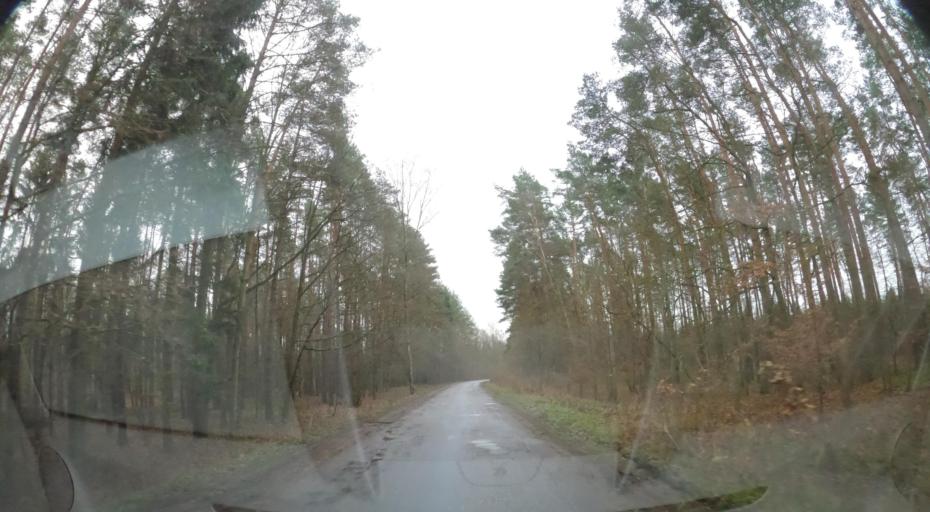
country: PL
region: Greater Poland Voivodeship
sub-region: Powiat zlotowski
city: Krajenka
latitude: 53.2852
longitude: 17.0691
